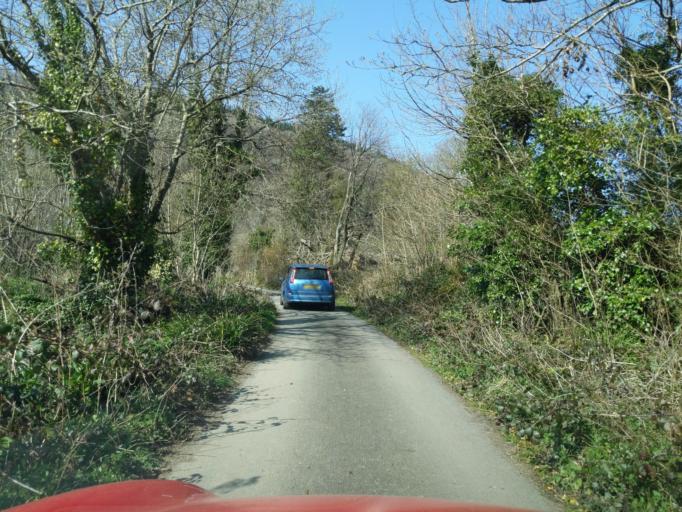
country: GB
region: England
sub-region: Devon
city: Bere Alston
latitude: 50.4613
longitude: -4.1545
